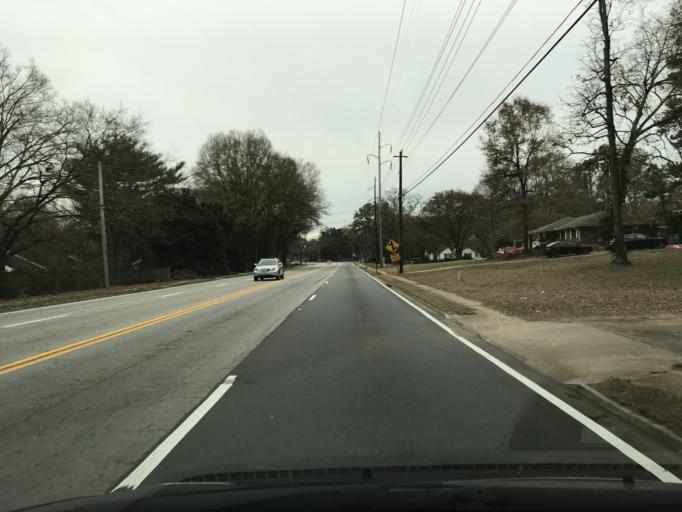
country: US
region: Georgia
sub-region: DeKalb County
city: Tucker
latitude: 33.8766
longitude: -84.2182
